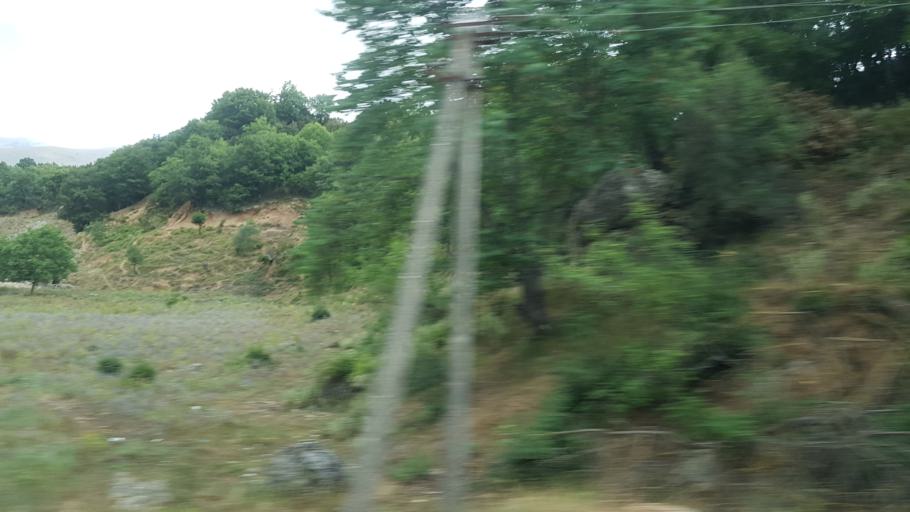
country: AL
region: Vlore
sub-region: Rrethi i Sarandes
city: Dhiver
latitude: 39.9120
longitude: 20.1860
